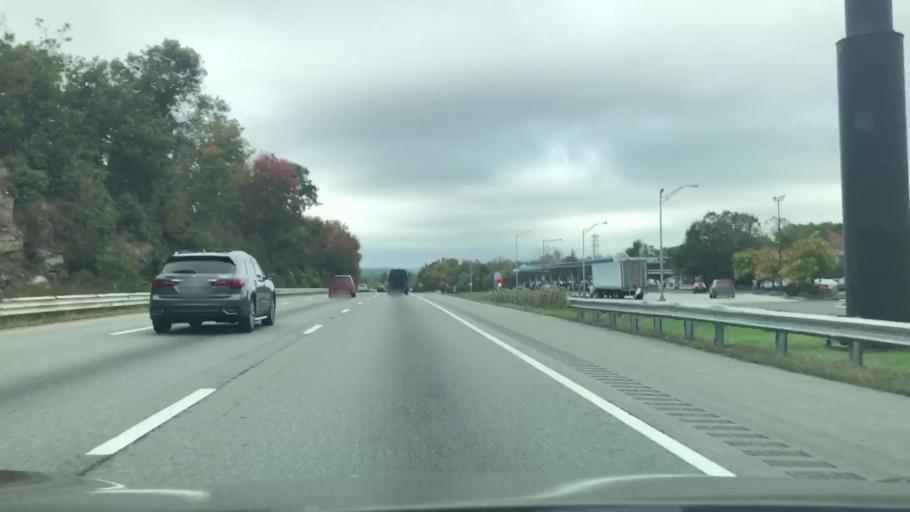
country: US
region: Massachusetts
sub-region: Worcester County
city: Charlton
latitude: 42.1398
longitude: -72.0269
